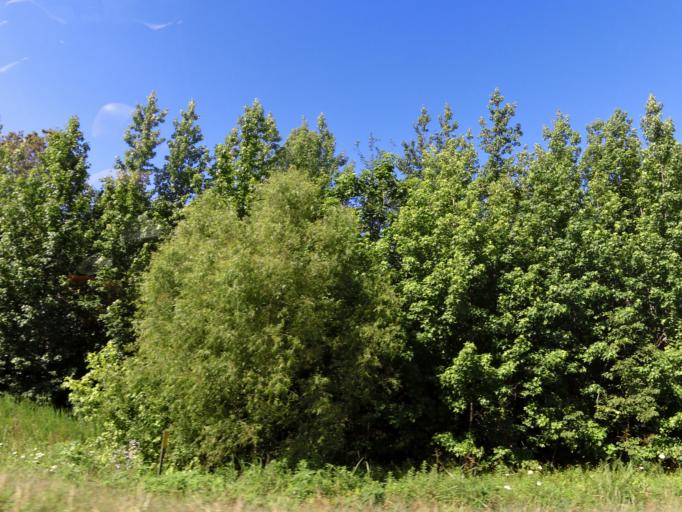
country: US
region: Arkansas
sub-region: Clay County
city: Piggott
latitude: 36.4102
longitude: -90.2210
